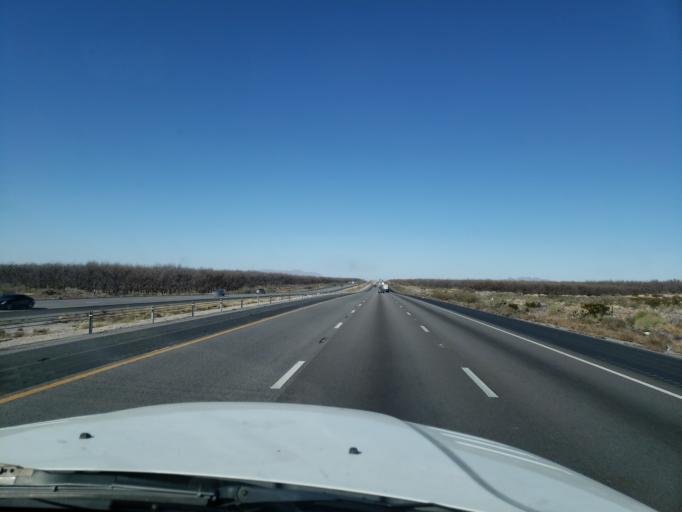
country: US
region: New Mexico
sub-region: Dona Ana County
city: Mesquite
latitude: 32.2229
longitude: -106.7048
